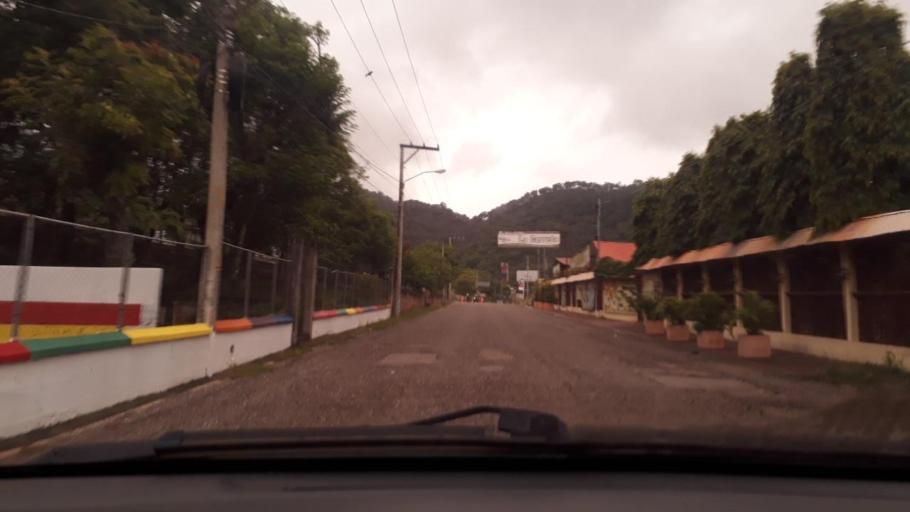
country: GT
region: Chiquimula
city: Esquipulas
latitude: 14.5618
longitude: -89.3552
